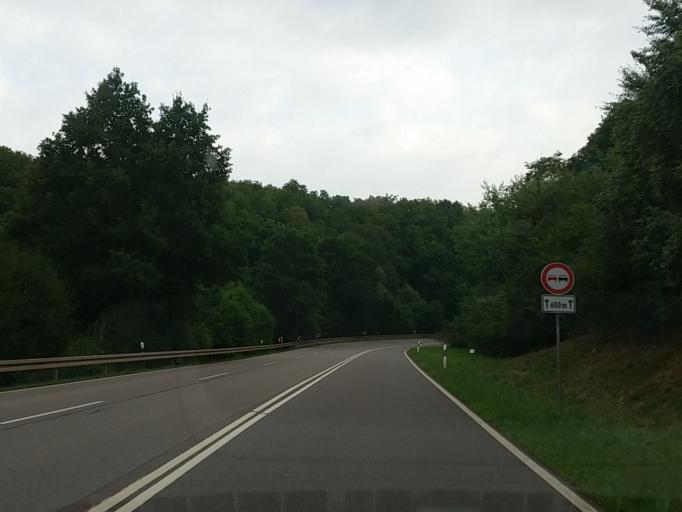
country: DE
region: Saarland
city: Schmelz
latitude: 49.4657
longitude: 6.8437
